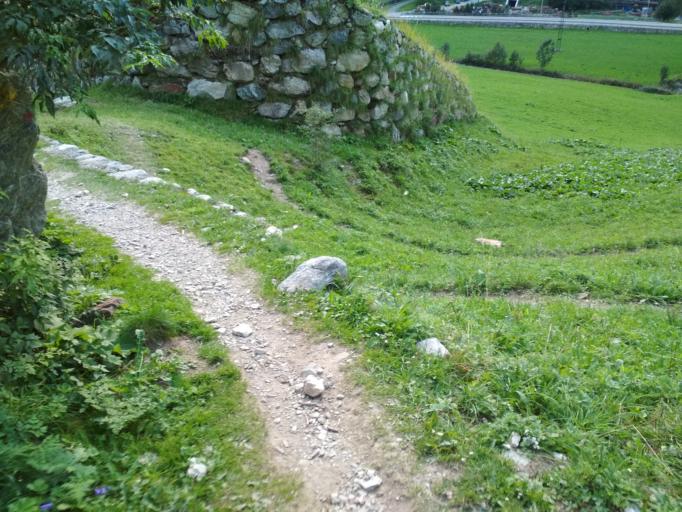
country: IT
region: Aosta Valley
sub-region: Valle d'Aosta
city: Gressoney-Saint-Jean
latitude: 45.7956
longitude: 7.8252
